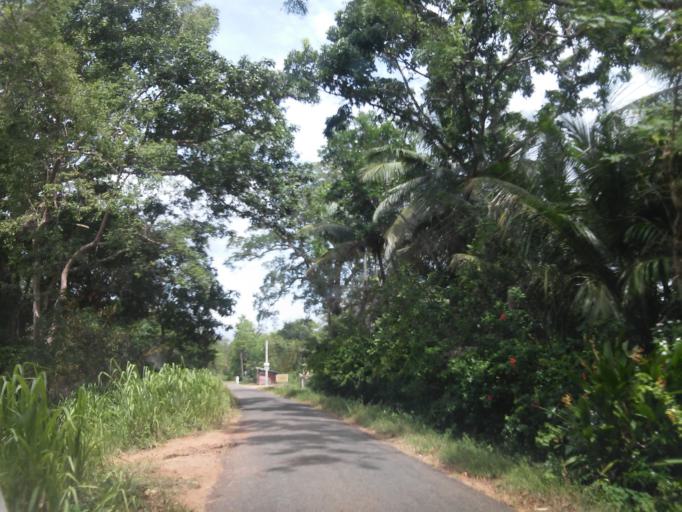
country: LK
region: Central
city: Sigiriya
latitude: 8.0882
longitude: 80.6752
